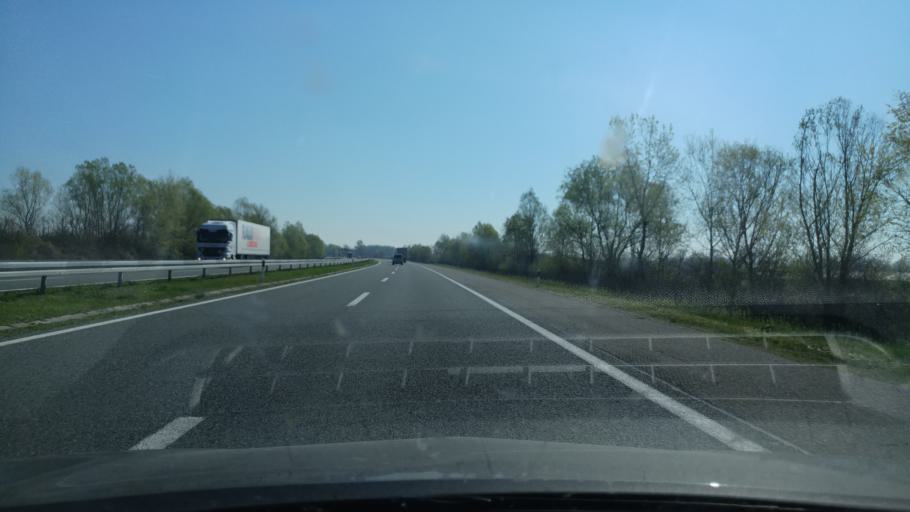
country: HR
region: Brodsko-Posavska
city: Garcin
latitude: 45.1559
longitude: 18.1910
